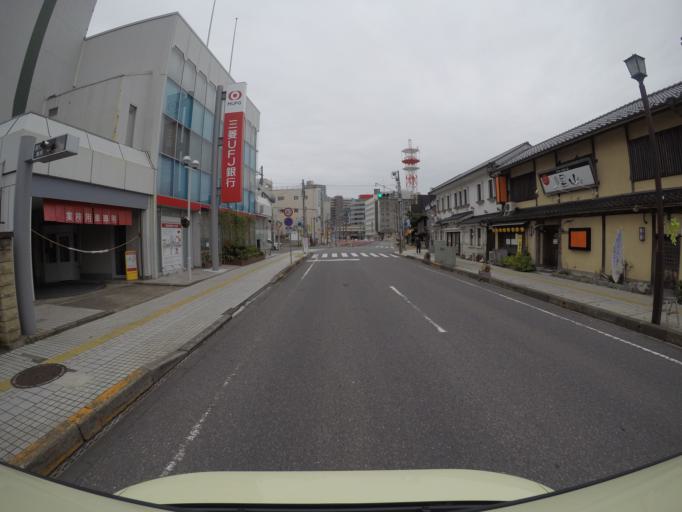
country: JP
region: Ibaraki
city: Naka
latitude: 36.0831
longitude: 140.2008
